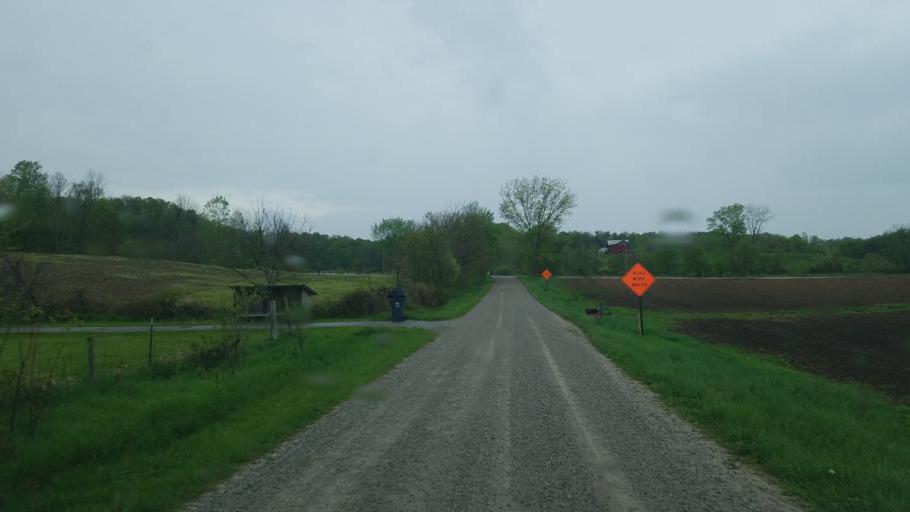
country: US
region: Ohio
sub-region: Knox County
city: Fredericktown
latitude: 40.5121
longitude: -82.6682
